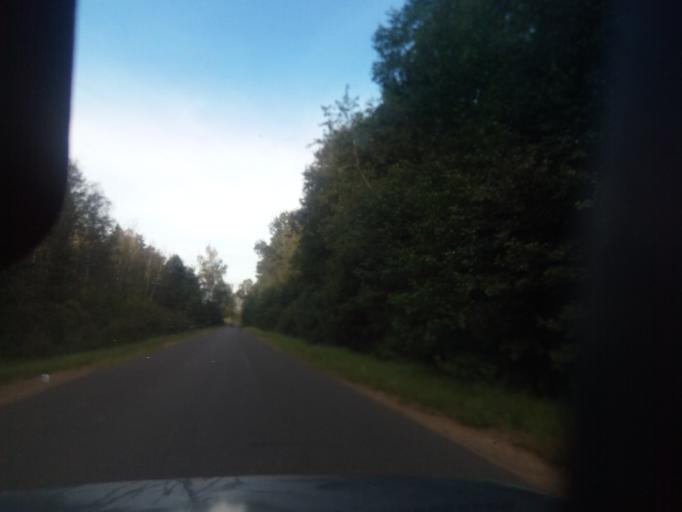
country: BY
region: Vitebsk
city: Dzisna
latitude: 55.6430
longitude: 28.3162
